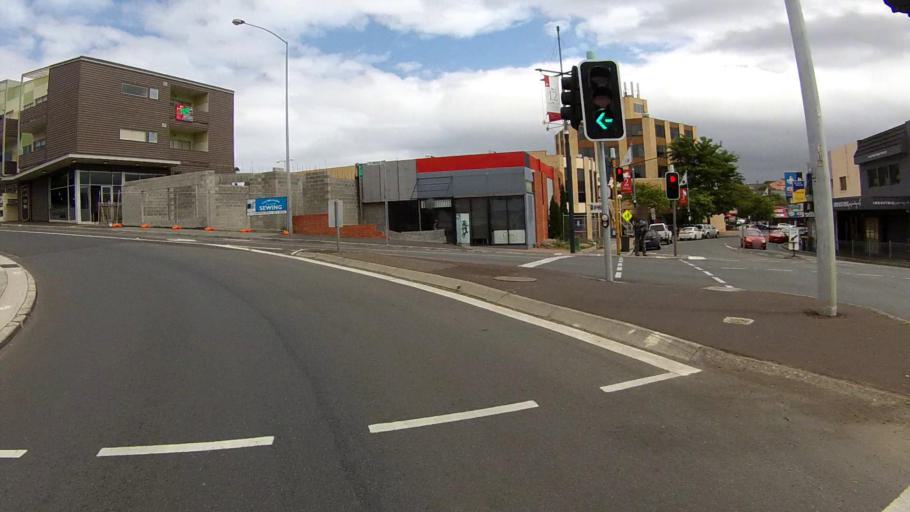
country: AU
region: Tasmania
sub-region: Clarence
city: Bellerive
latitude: -42.8741
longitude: 147.3685
